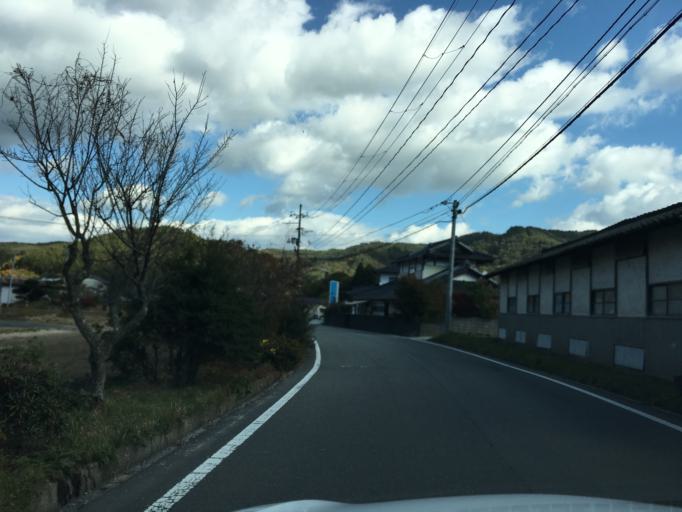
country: JP
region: Fukushima
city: Namie
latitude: 37.3355
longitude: 140.8032
